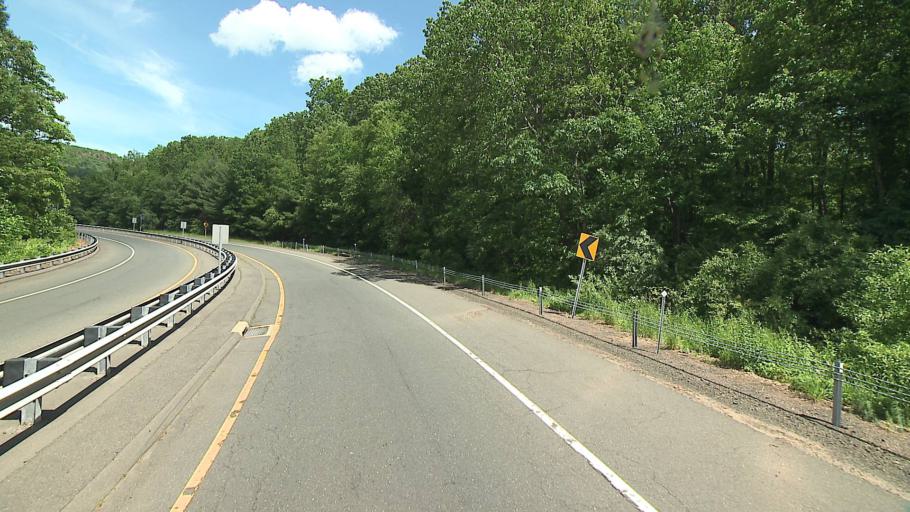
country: US
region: Connecticut
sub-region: New Haven County
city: Meriden
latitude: 41.5530
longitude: -72.8484
